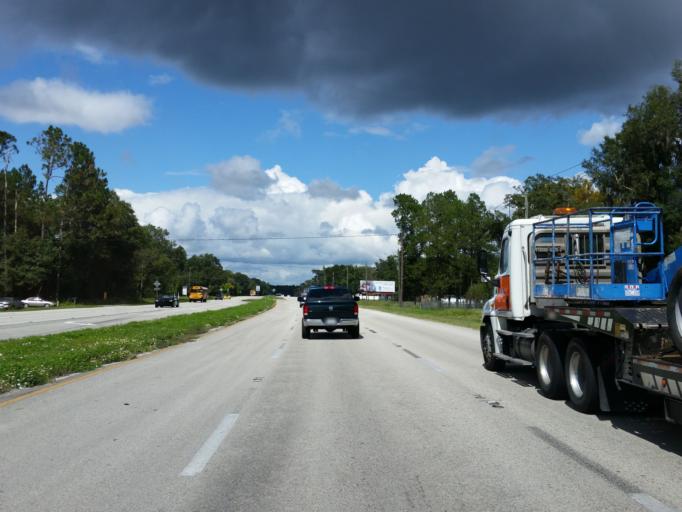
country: US
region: Florida
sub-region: Bradford County
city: Starke
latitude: 29.9008
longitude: -82.1365
